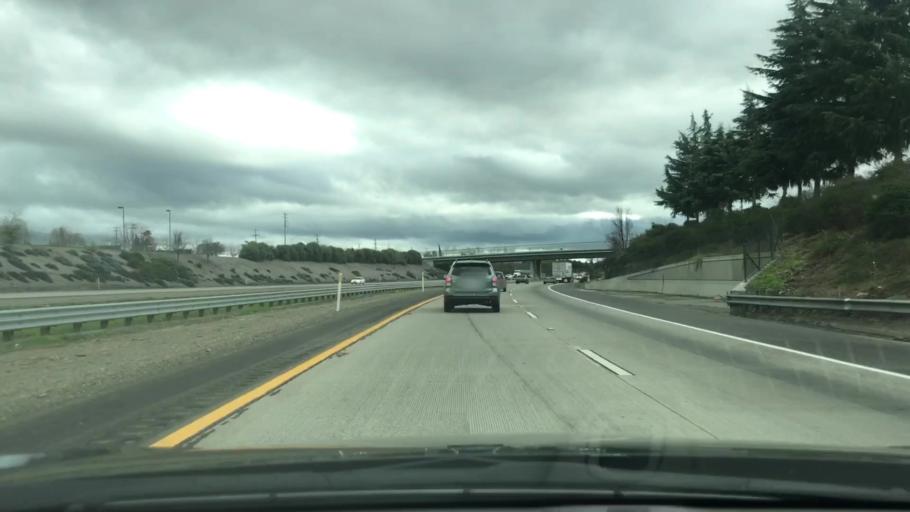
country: US
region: California
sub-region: Merced County
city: Livingston
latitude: 37.3886
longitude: -120.7252
